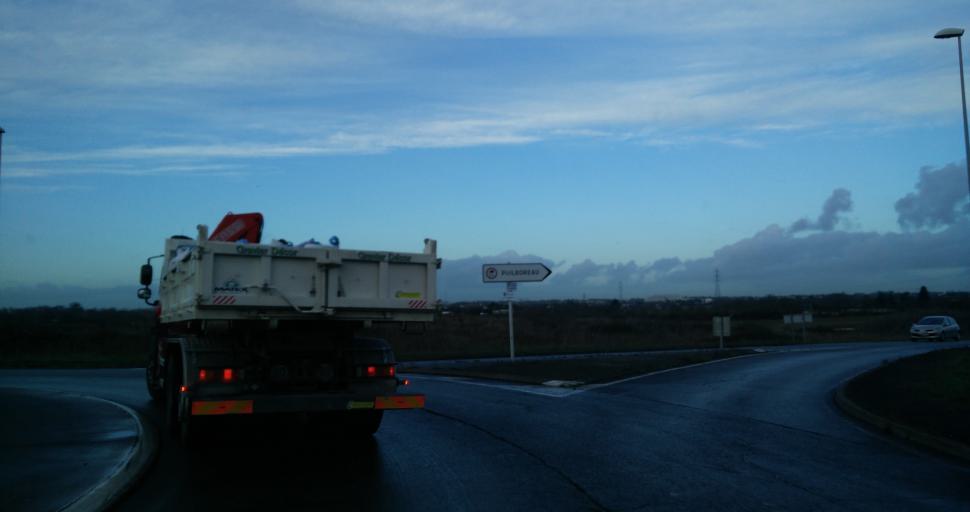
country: FR
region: Poitou-Charentes
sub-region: Departement de la Charente-Maritime
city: Puilboreau
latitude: 46.1793
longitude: -1.1230
